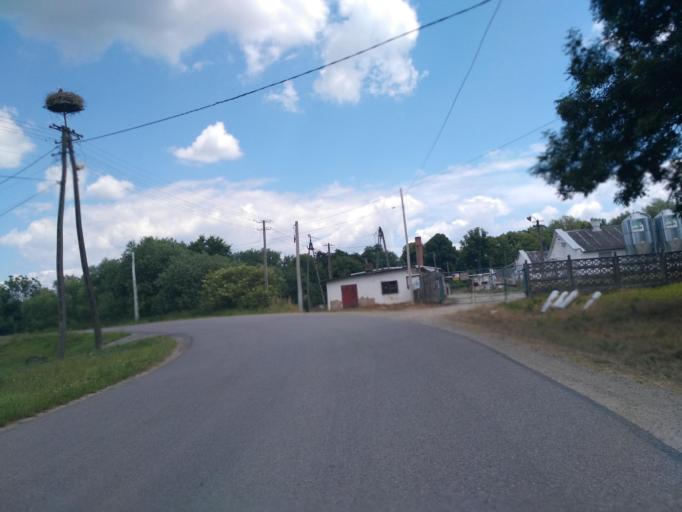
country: PL
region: Subcarpathian Voivodeship
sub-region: Powiat debicki
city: Brzostek
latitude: 49.8609
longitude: 21.4445
